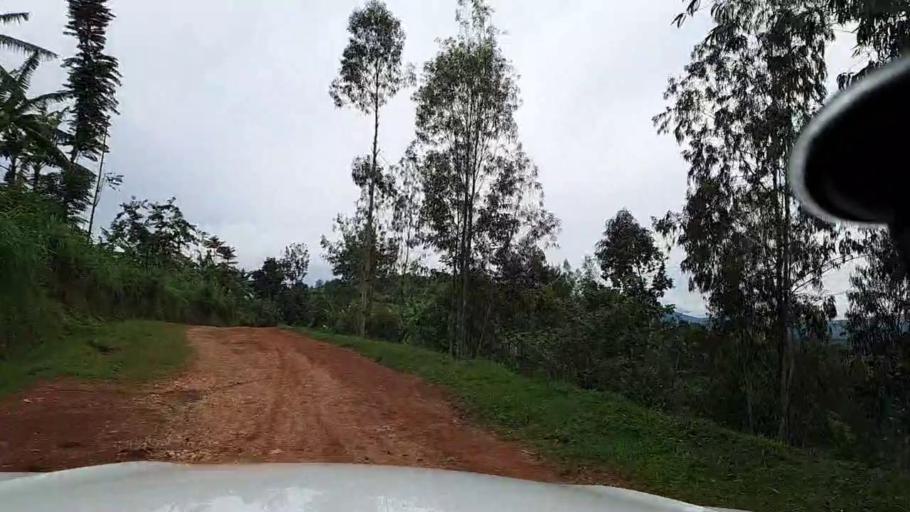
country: RW
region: Southern Province
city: Gitarama
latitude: -2.0870
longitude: 29.6358
